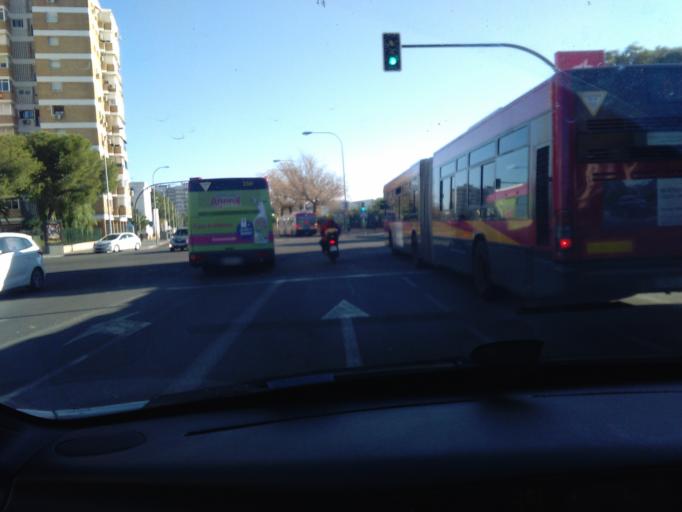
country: ES
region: Andalusia
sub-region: Provincia de Sevilla
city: Sevilla
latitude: 37.3938
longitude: -5.9626
